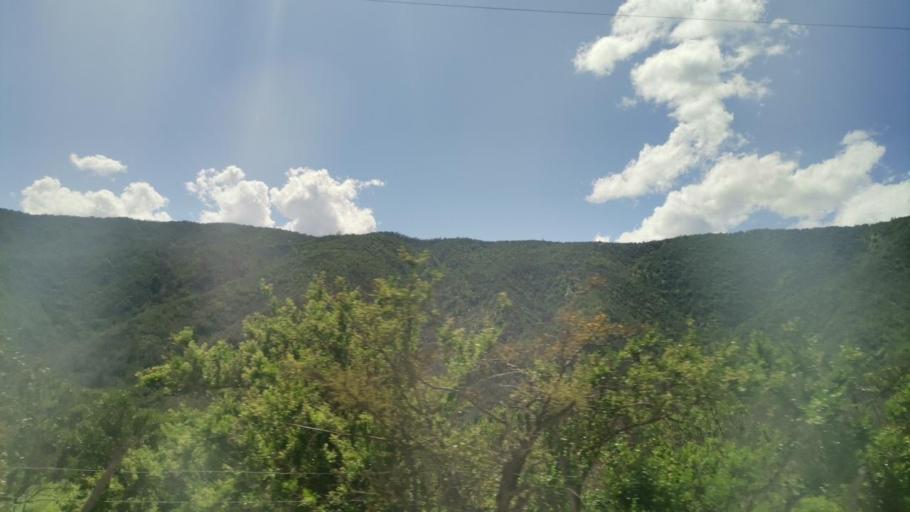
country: CL
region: Valparaiso
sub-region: Provincia de Marga Marga
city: Villa Alemana
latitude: -33.1911
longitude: -71.2864
